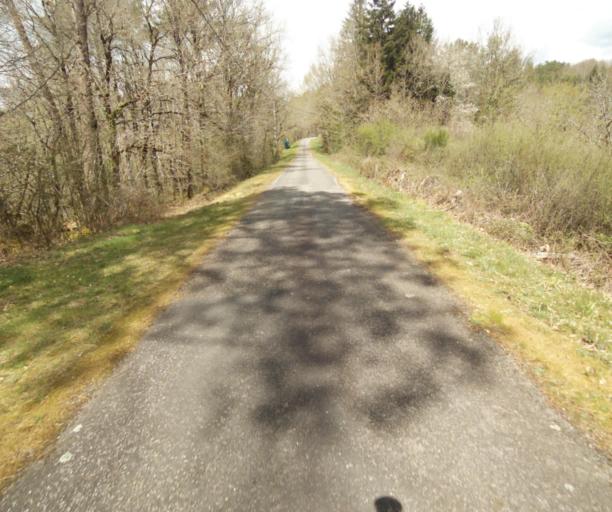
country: FR
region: Limousin
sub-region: Departement de la Correze
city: Sainte-Fortunade
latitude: 45.1783
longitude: 1.8710
